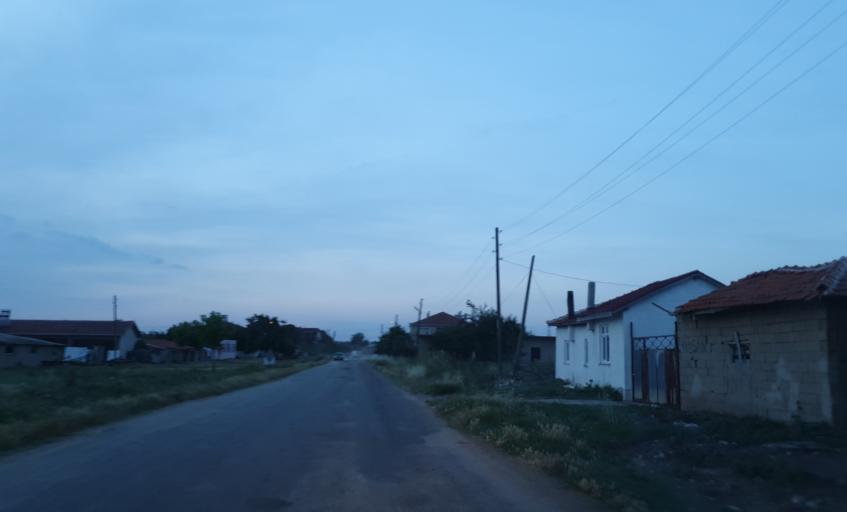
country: TR
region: Kirklareli
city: Vize
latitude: 41.4830
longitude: 27.7523
